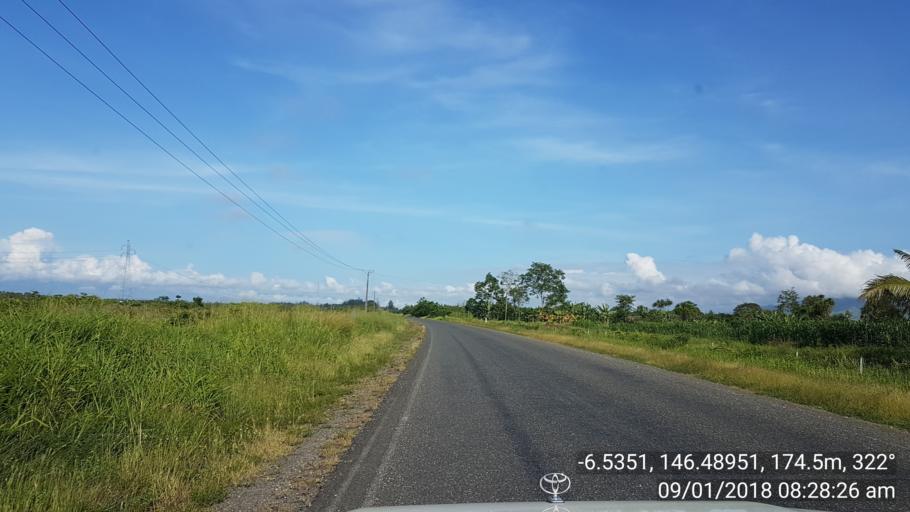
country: PG
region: Morobe
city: Lae
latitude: -6.5348
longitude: 146.4889
